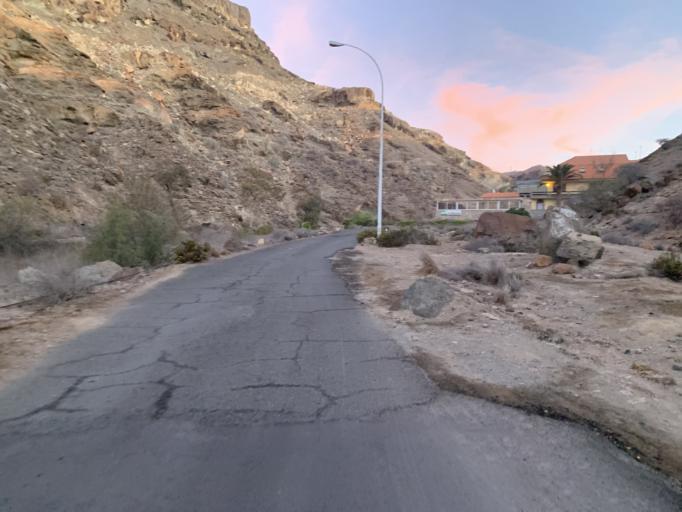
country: ES
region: Canary Islands
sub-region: Provincia de Las Palmas
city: Puerto Rico
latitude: 27.8043
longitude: -15.7317
